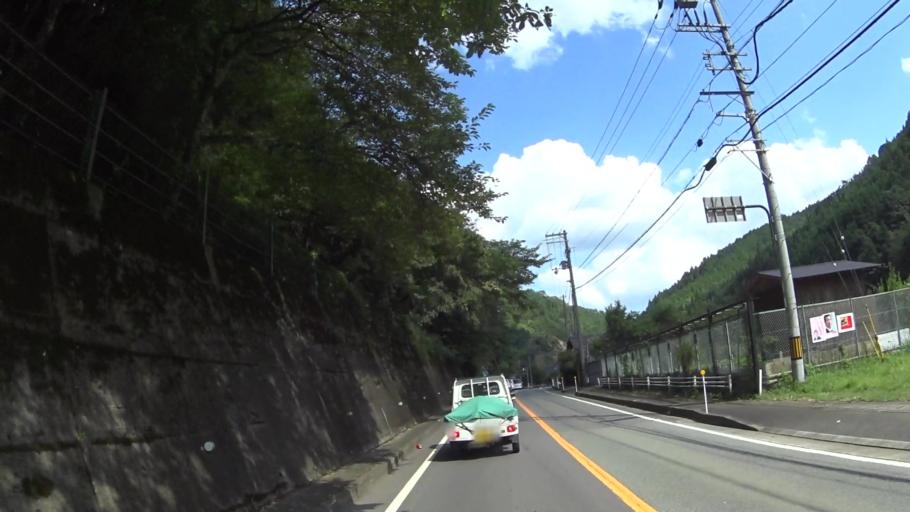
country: JP
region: Kyoto
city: Kameoka
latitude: 35.1212
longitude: 135.6498
